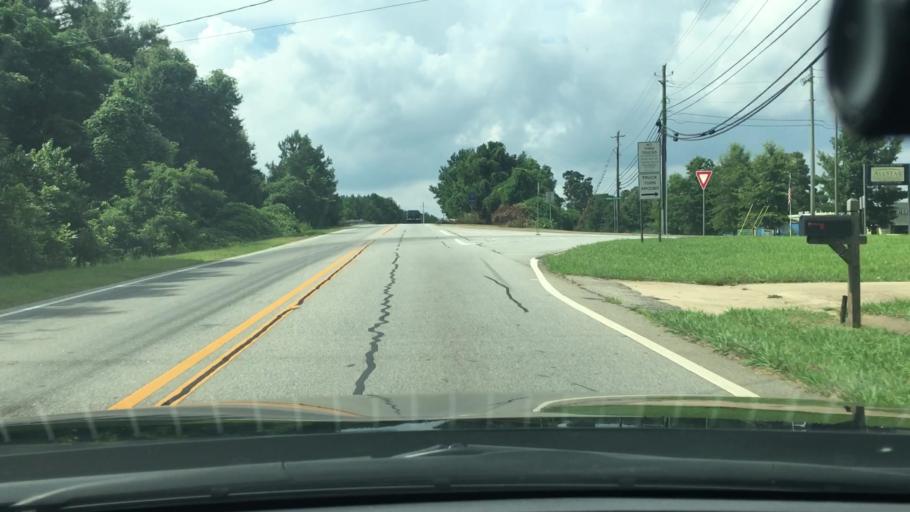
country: US
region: Georgia
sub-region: Coweta County
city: East Newnan
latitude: 33.3516
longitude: -84.7897
